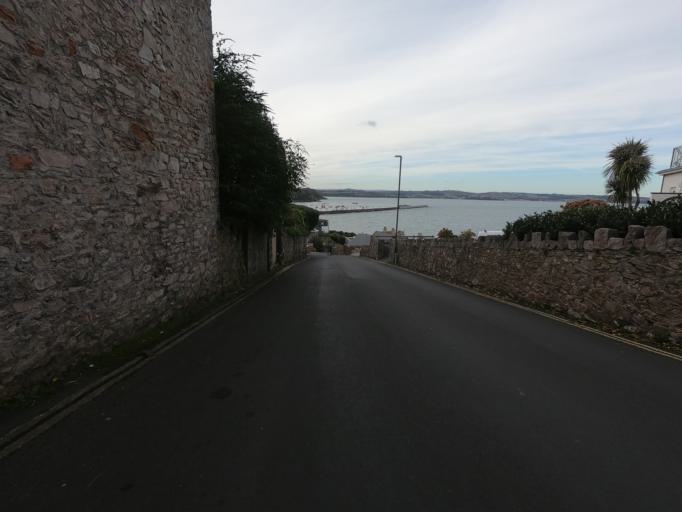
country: GB
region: England
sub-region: Borough of Torbay
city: Brixham
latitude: 50.3999
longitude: -3.4974
